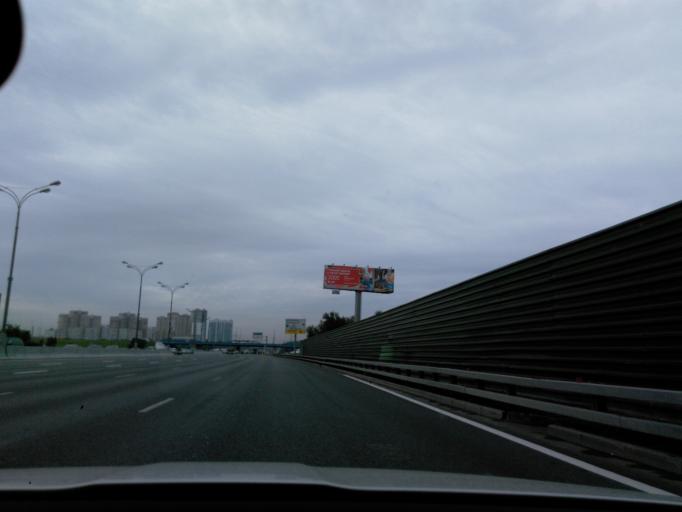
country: RU
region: Moscow
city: Gol'yanovo
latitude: 55.8182
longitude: 37.8379
